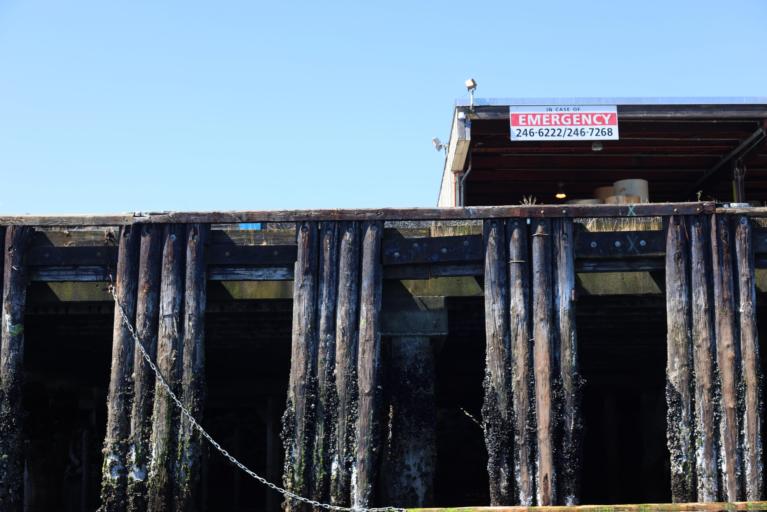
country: CA
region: British Columbia
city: North Cowichan
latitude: 48.8718
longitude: -123.6411
